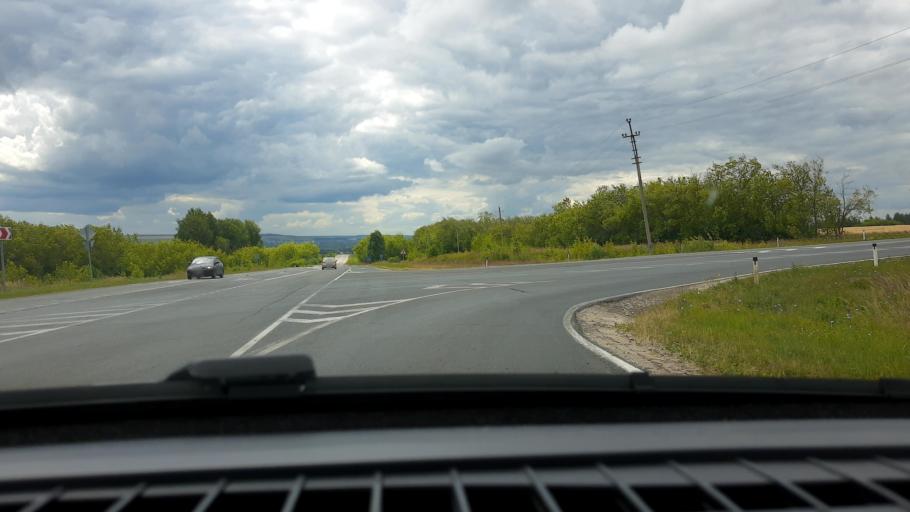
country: RU
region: Nizjnij Novgorod
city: Sergach
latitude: 55.5491
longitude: 45.5778
